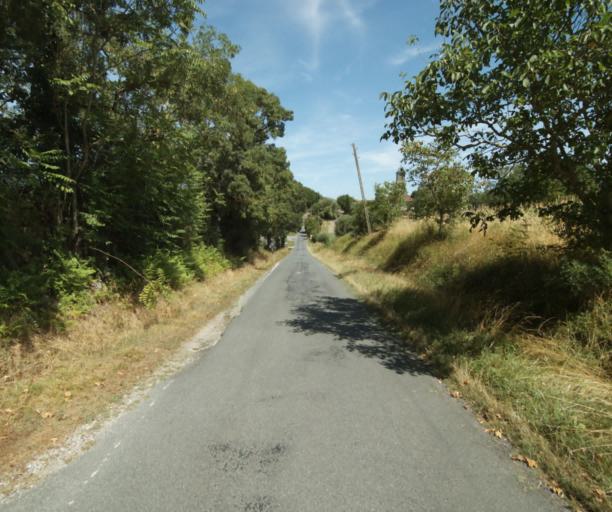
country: FR
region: Midi-Pyrenees
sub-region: Departement du Tarn
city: Puylaurens
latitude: 43.5272
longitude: 2.0047
